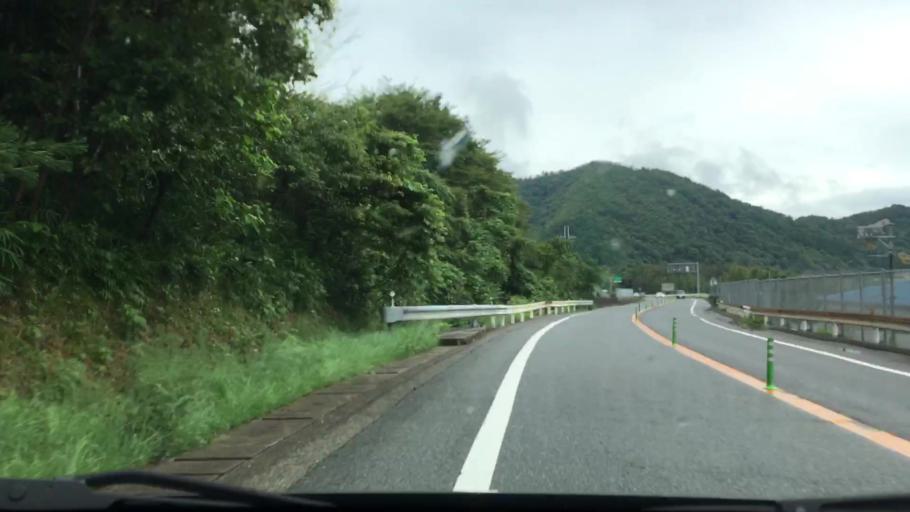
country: JP
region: Hyogo
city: Himeji
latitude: 35.0077
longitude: 134.7641
